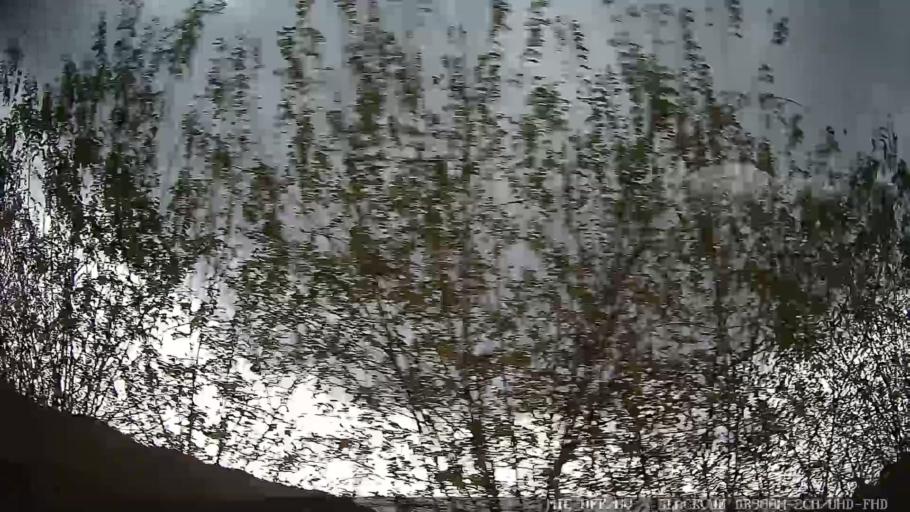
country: BR
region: Sao Paulo
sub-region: Itatiba
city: Itatiba
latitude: -23.0122
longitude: -46.9020
